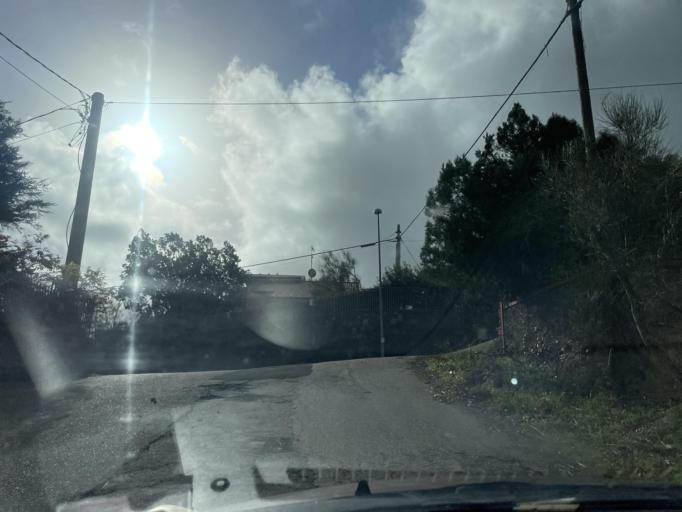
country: IT
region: Sicily
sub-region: Catania
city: Nicolosi
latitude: 37.6287
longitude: 15.0210
